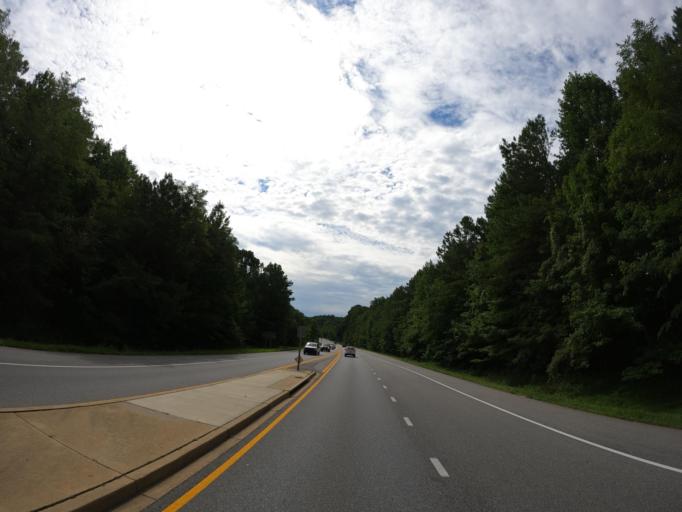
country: US
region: Maryland
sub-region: Saint Mary's County
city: Leonardtown
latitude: 38.2887
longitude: -76.6242
